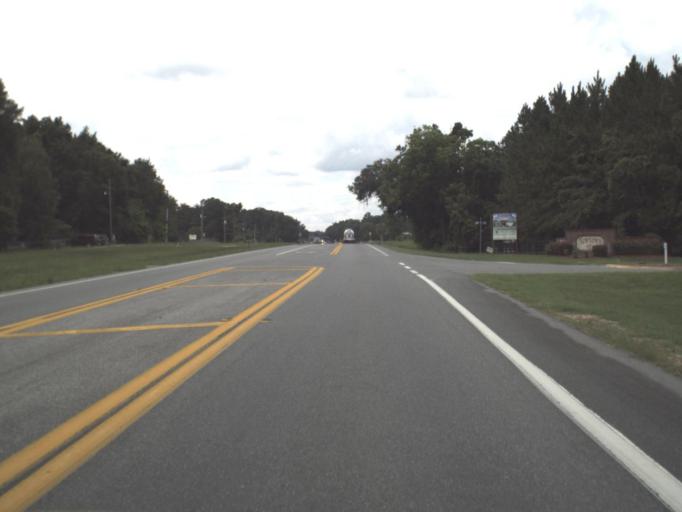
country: US
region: Florida
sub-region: Alachua County
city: Newberry
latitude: 29.6617
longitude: -82.6070
